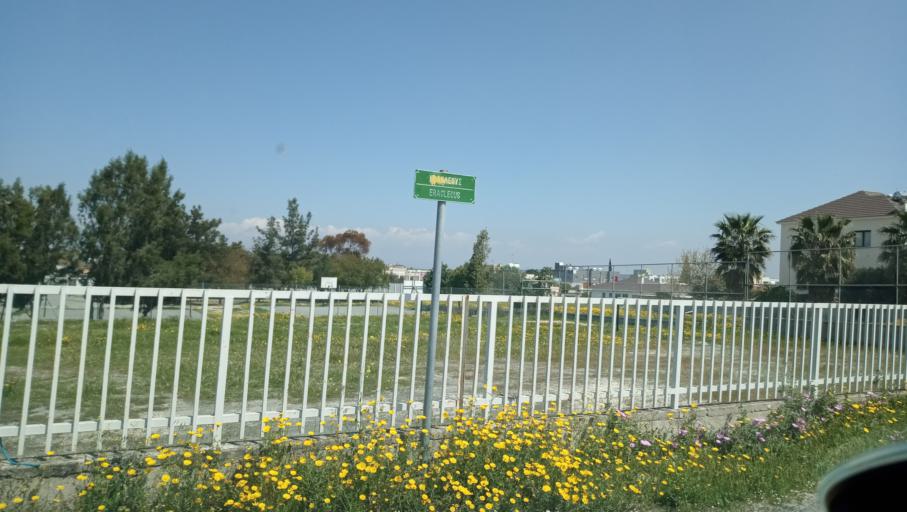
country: CY
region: Lefkosia
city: Dali
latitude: 35.0141
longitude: 33.3997
